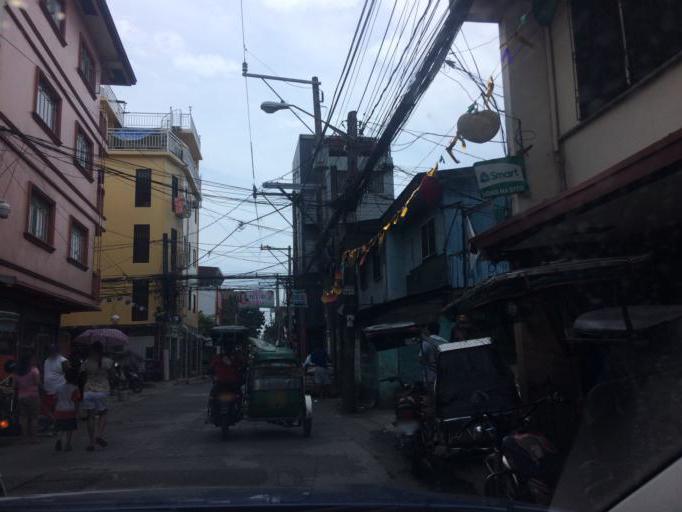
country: PH
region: Metro Manila
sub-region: Makati City
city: Makati City
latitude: 14.5431
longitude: 121.0031
